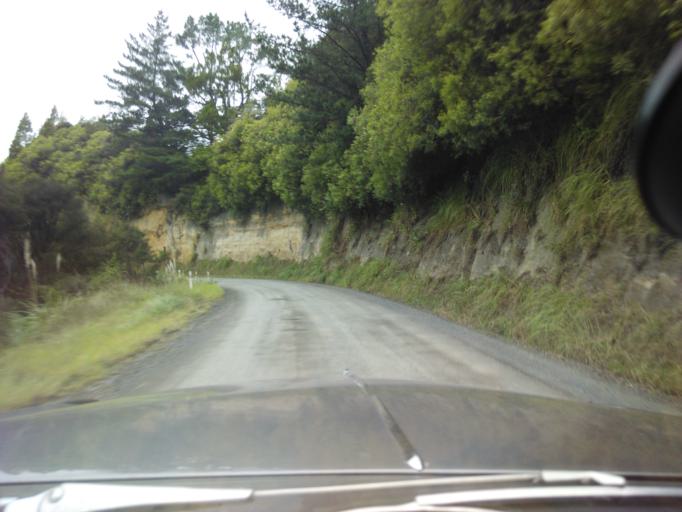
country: NZ
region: Auckland
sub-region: Auckland
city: Warkworth
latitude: -36.5319
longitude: 174.6370
